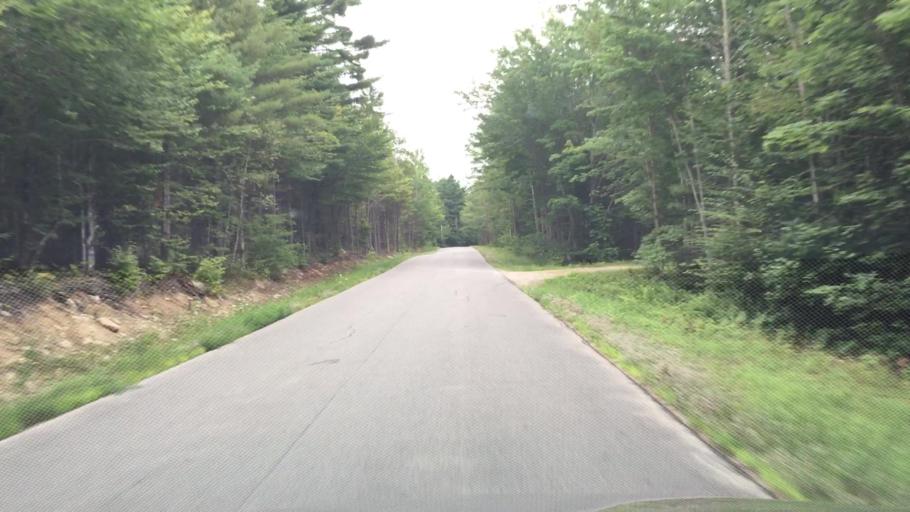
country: US
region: Maine
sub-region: Waldo County
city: Stockton Springs
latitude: 44.5201
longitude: -68.8790
